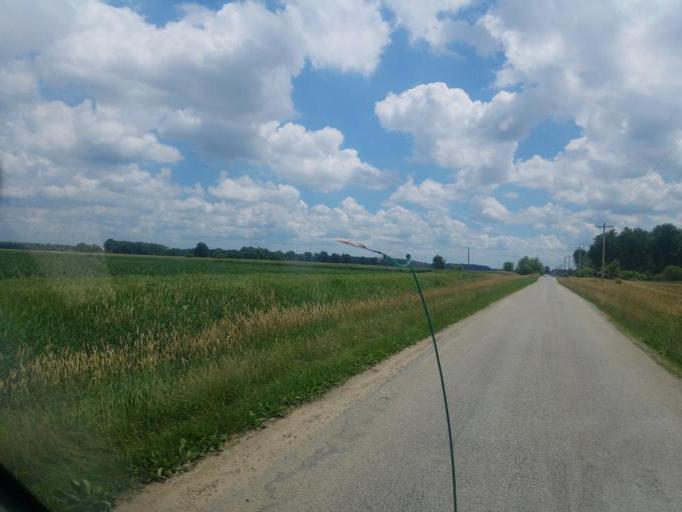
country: US
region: Ohio
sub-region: Huron County
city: Willard
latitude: 41.0359
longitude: -82.8309
